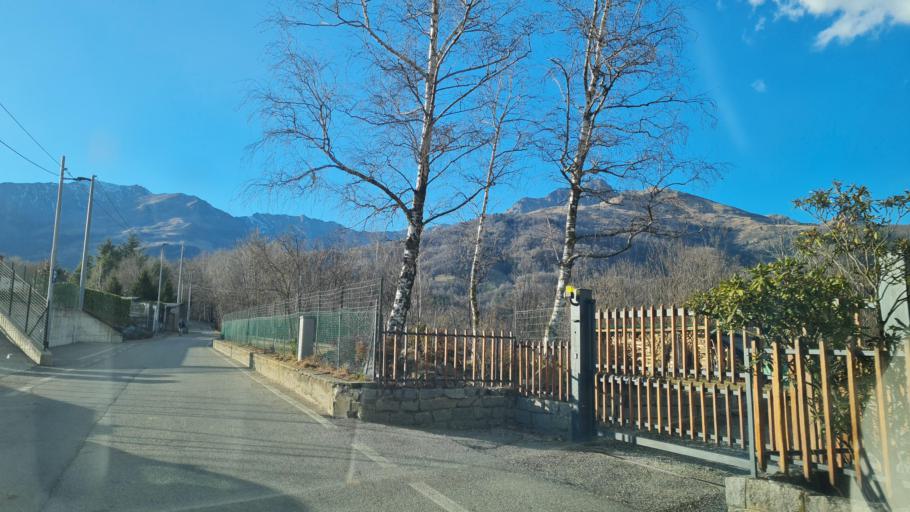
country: IT
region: Piedmont
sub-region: Provincia di Biella
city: Occhieppo Superiore
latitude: 45.5711
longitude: 8.0017
